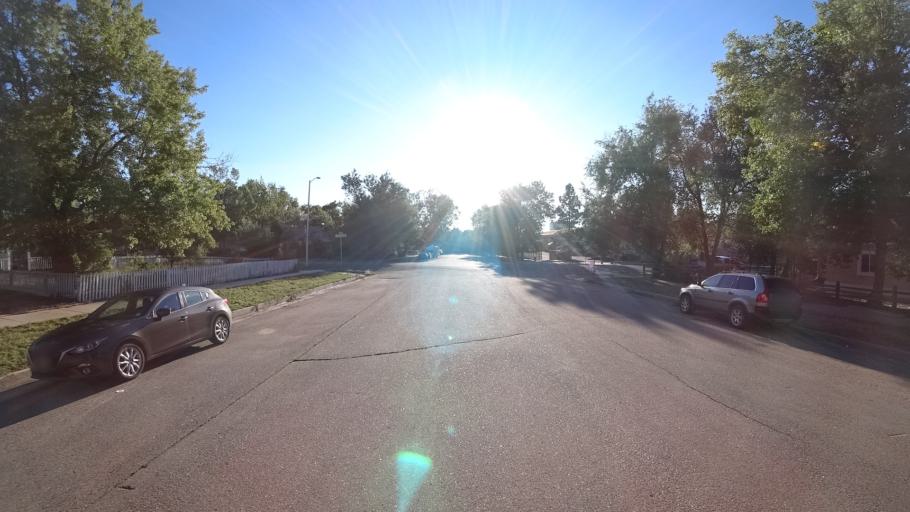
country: US
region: Colorado
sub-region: El Paso County
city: Colorado Springs
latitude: 38.8384
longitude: -104.8329
